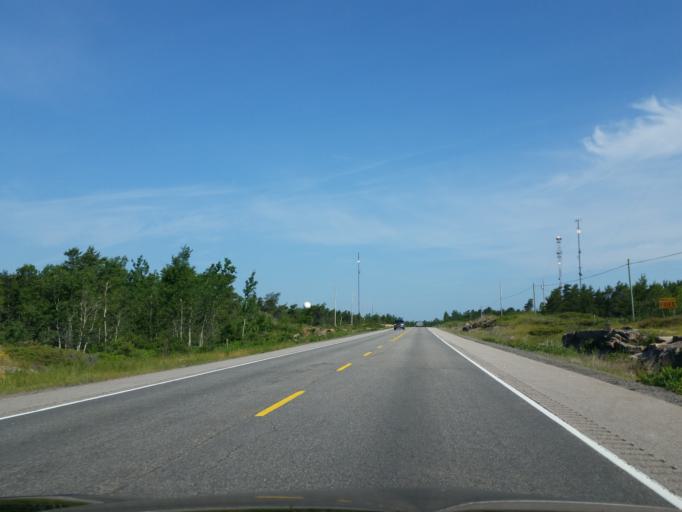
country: CA
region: Ontario
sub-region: Parry Sound District
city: Parry Sound
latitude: 45.7878
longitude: -80.5253
